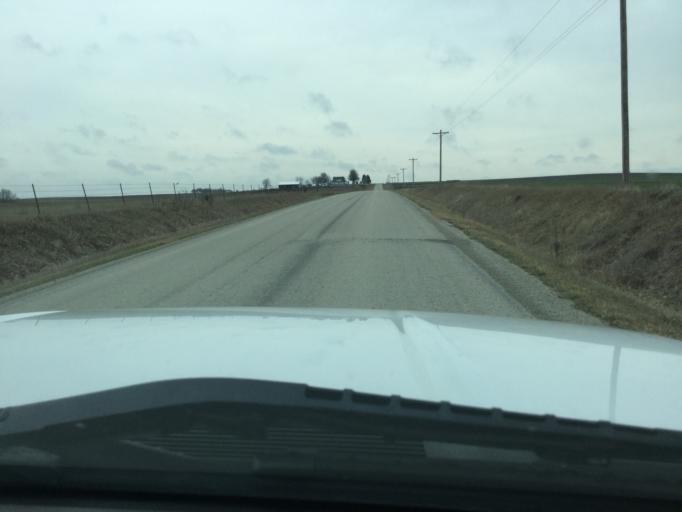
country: US
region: Kansas
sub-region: Nemaha County
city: Sabetha
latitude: 39.8582
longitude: -95.7142
